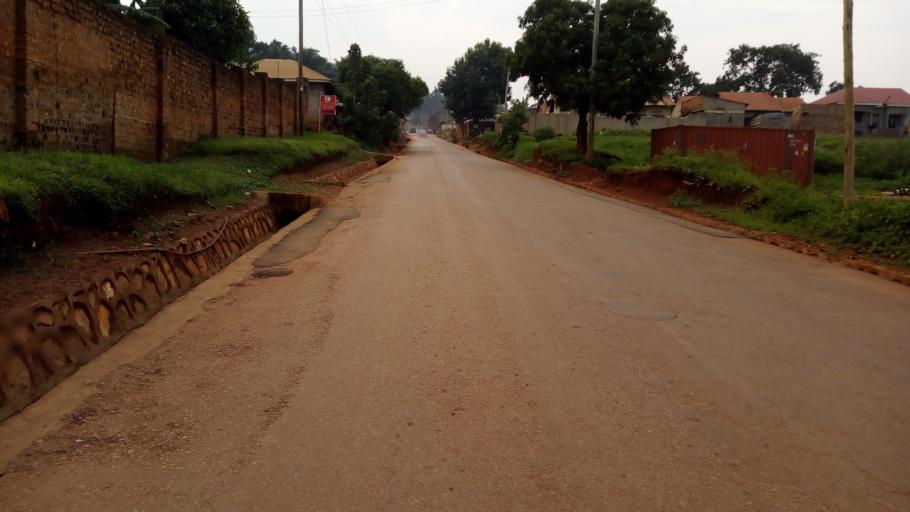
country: UG
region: Central Region
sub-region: Wakiso District
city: Kireka
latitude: 0.3197
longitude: 32.6328
